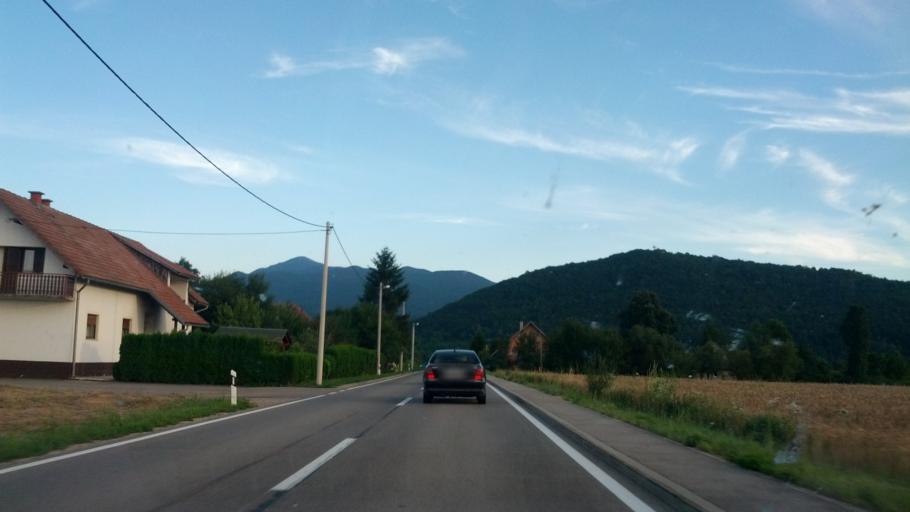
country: BA
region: Federation of Bosnia and Herzegovina
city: Izacic
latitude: 44.8995
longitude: 15.7242
